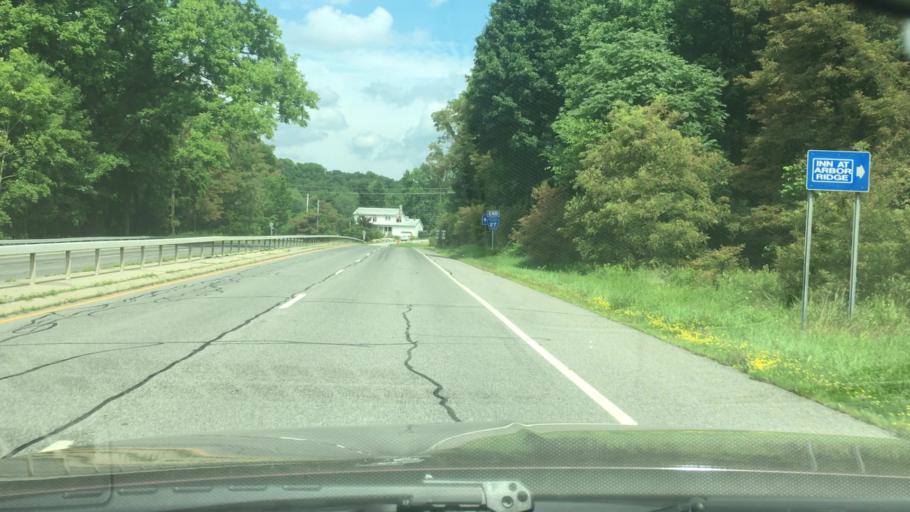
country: US
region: New York
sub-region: Dutchess County
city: Brinckerhoff
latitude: 41.5459
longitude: -73.8176
